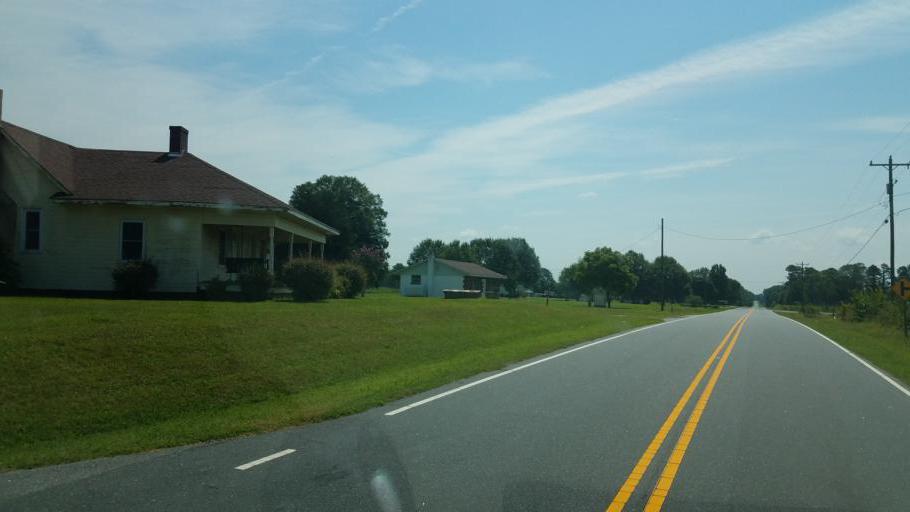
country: US
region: North Carolina
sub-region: Gaston County
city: Cherryville
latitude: 35.5186
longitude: -81.4788
